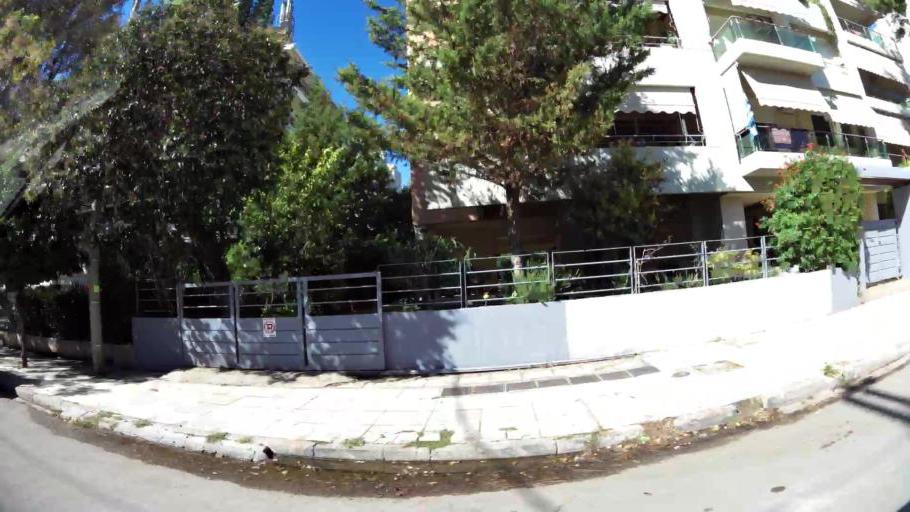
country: GR
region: Attica
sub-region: Nomarchia Athinas
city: Khalandrion
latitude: 38.0346
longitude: 23.8124
